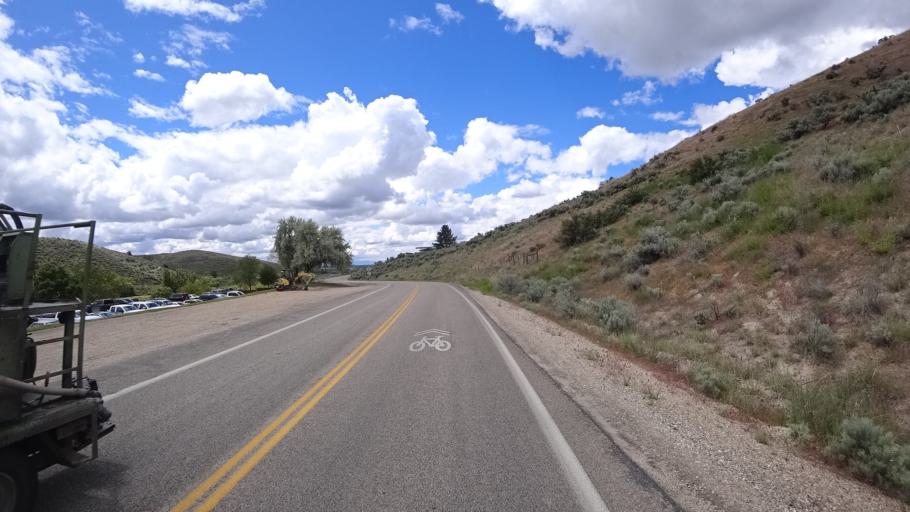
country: US
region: Idaho
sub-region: Ada County
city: Garden City
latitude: 43.6637
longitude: -116.2236
